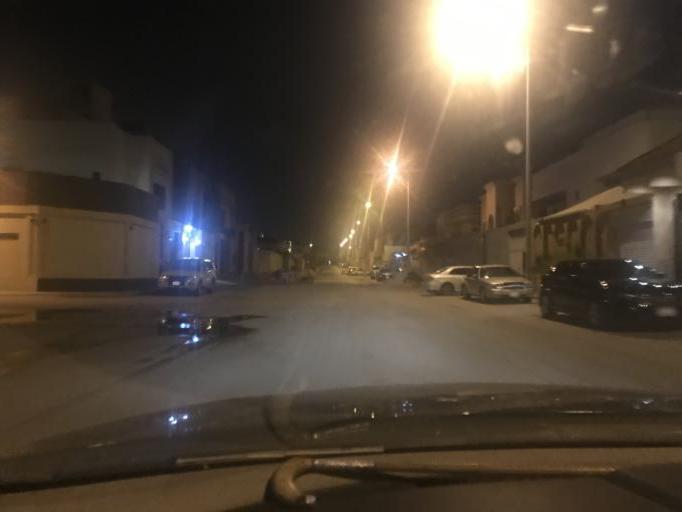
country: SA
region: Ar Riyad
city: Riyadh
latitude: 24.7564
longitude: 46.7631
